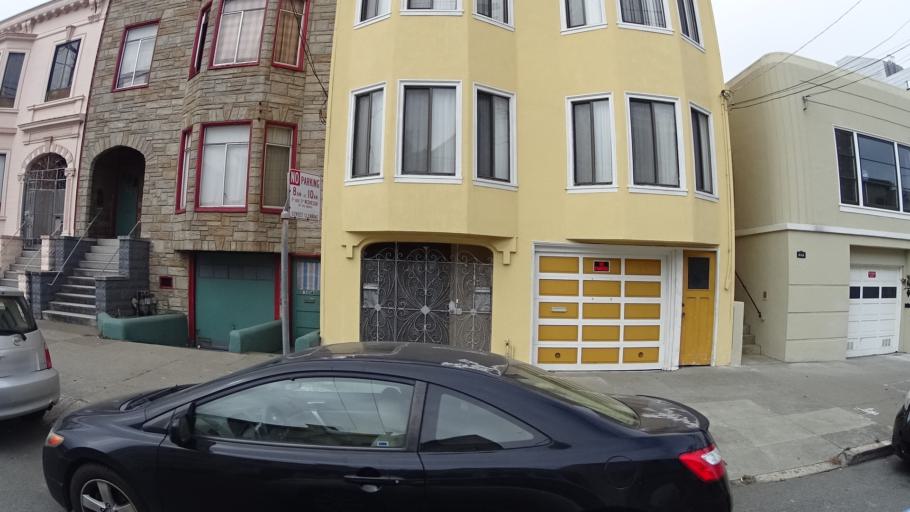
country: US
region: California
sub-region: San Francisco County
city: San Francisco
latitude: 37.7779
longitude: -122.4640
